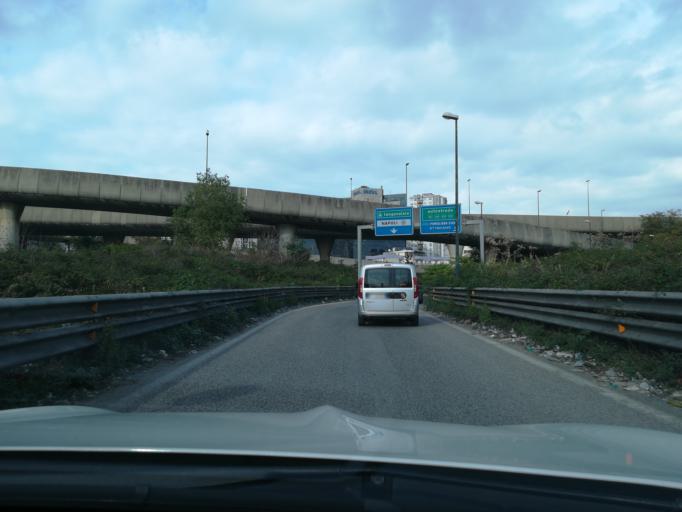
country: IT
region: Campania
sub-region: Provincia di Napoli
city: Casavatore
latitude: 40.8626
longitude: 14.2876
